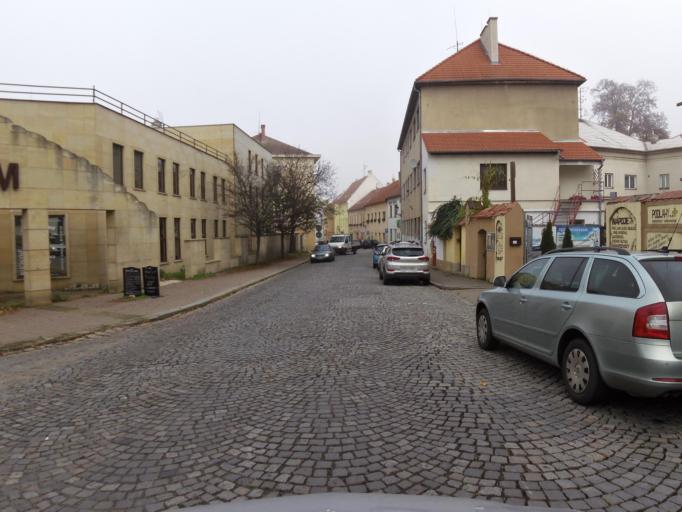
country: CZ
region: Ustecky
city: Zatec
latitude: 50.3242
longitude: 13.5436
